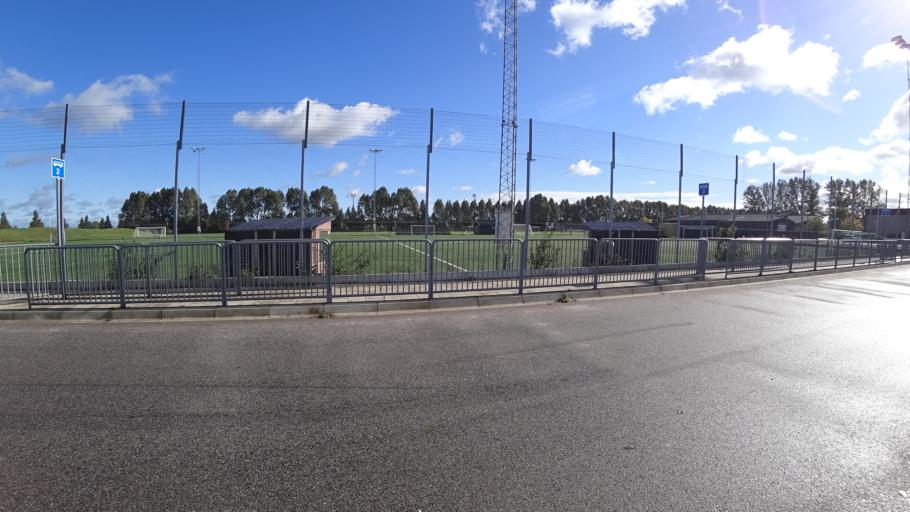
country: SE
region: Skane
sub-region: Kavlinge Kommun
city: Loddekopinge
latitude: 55.7661
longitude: 13.0173
